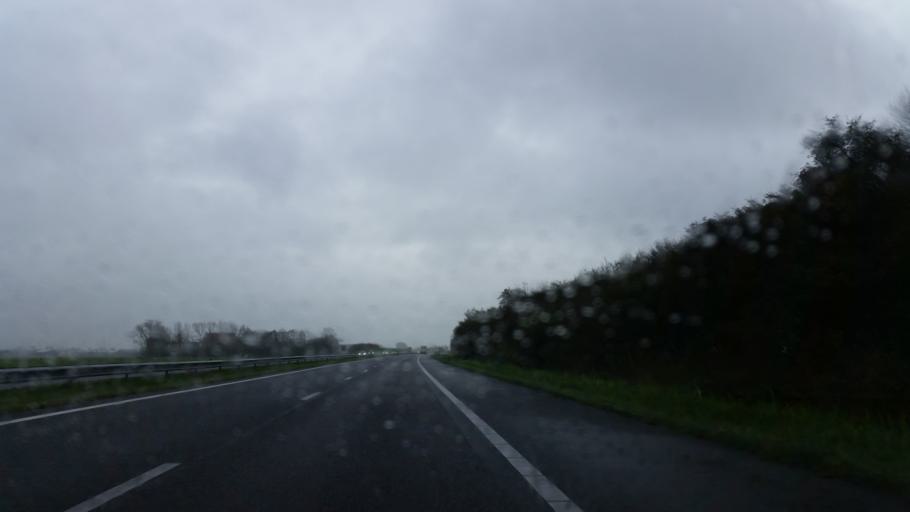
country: NL
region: Friesland
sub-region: Gemeente Boarnsterhim
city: Reduzum
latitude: 53.1106
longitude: 5.8136
